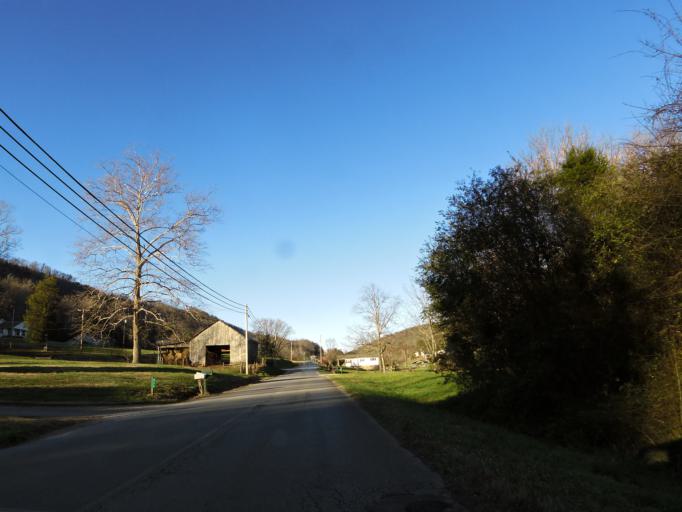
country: US
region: Tennessee
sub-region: Anderson County
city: Rocky Top
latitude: 36.1817
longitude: -84.1609
